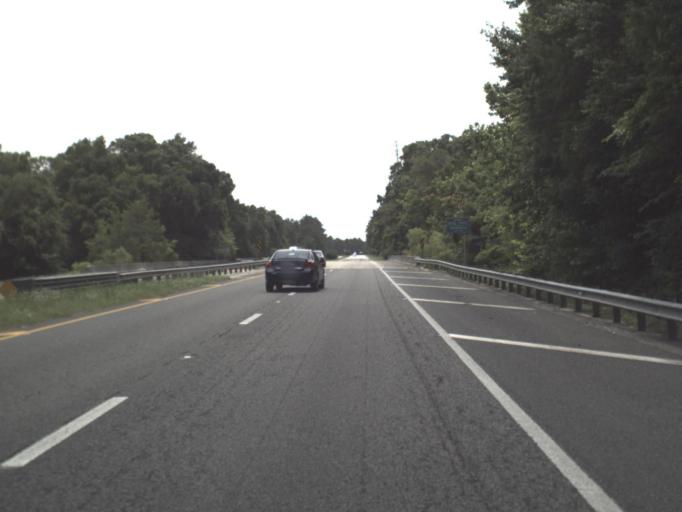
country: US
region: Florida
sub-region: Nassau County
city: Nassau Village-Ratliff
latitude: 30.5068
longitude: -81.7921
